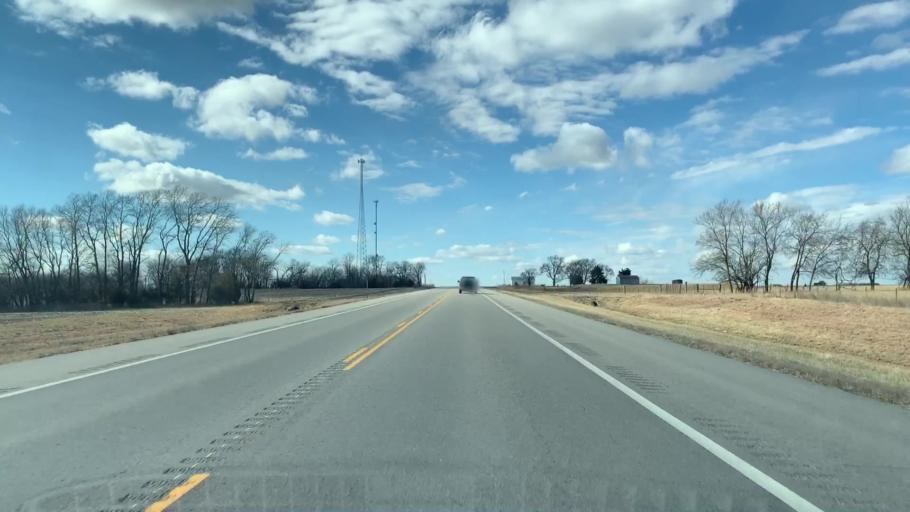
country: US
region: Kansas
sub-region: Labette County
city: Oswego
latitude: 37.3401
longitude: -95.0215
